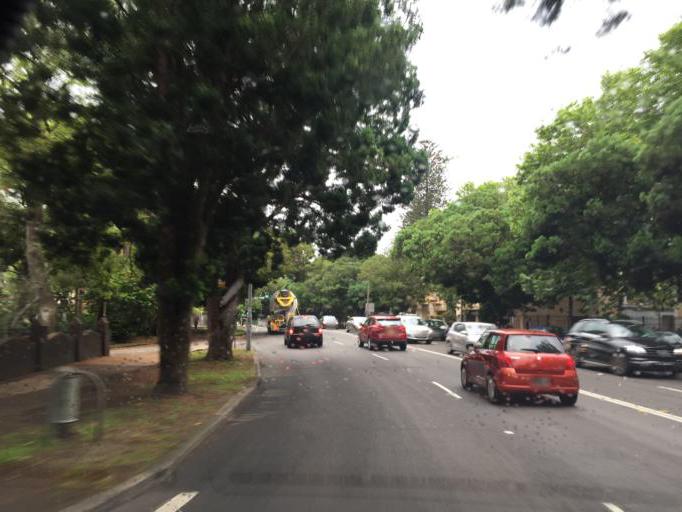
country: AU
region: New South Wales
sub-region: Woollahra
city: Point Piper
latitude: -33.8721
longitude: 151.2504
